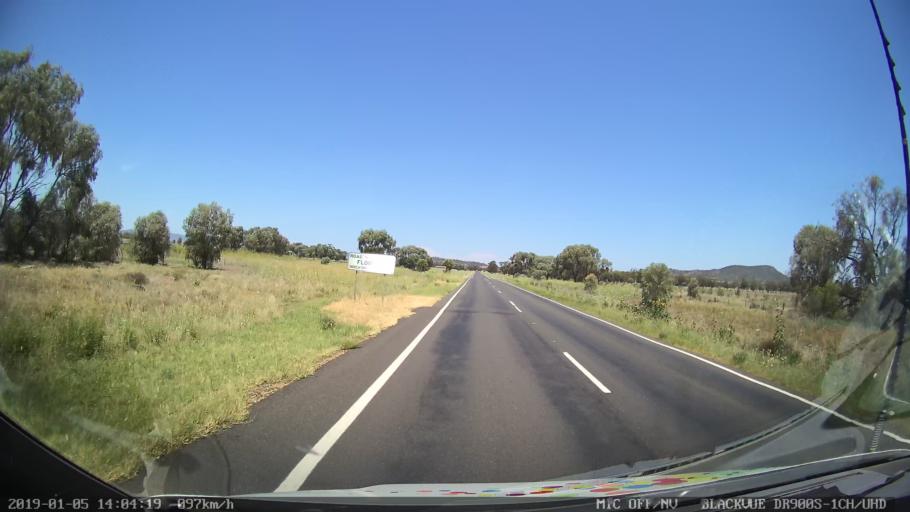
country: AU
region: New South Wales
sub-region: Gunnedah
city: Gunnedah
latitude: -31.1988
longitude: 150.3623
